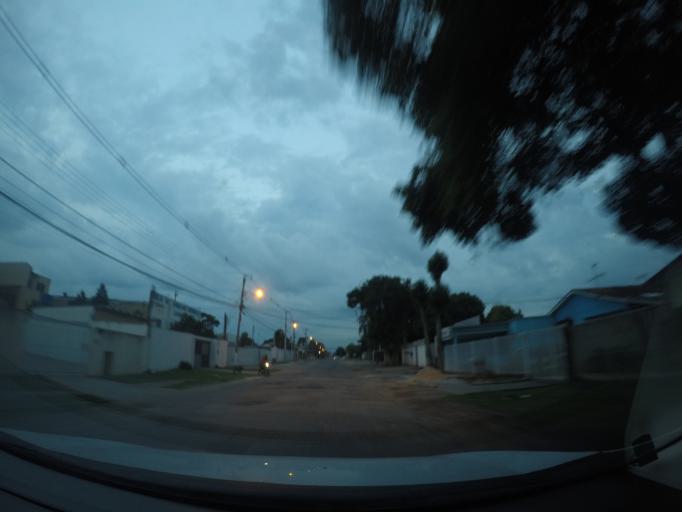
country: BR
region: Parana
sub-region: Sao Jose Dos Pinhais
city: Sao Jose dos Pinhais
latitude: -25.4963
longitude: -49.2346
